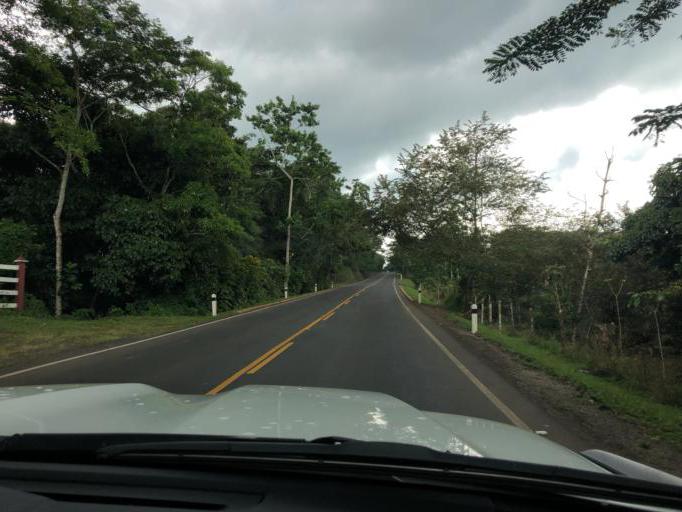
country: NI
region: Chontales
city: Villa Sandino
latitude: 11.9903
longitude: -84.8152
